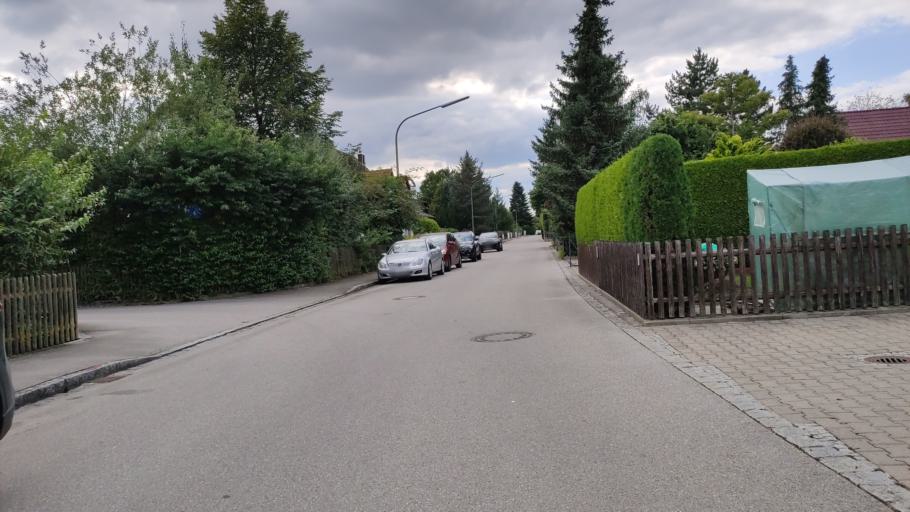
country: DE
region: Bavaria
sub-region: Swabia
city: Konigsbrunn
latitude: 48.2526
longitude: 10.8996
